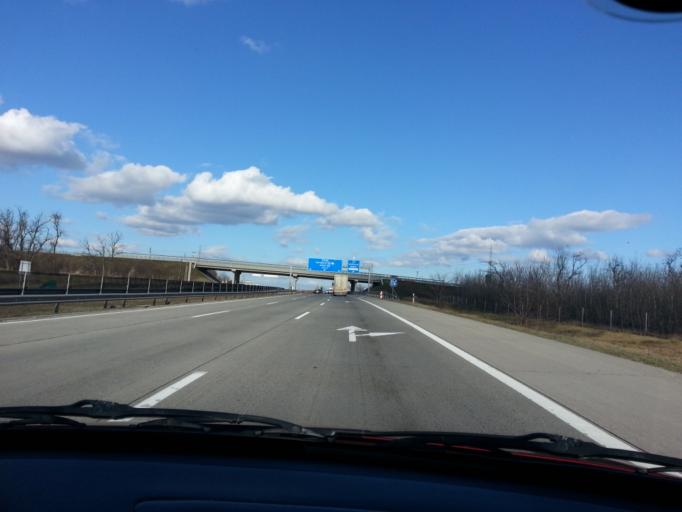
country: HU
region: Pest
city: Ecser
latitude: 47.4624
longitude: 19.3312
